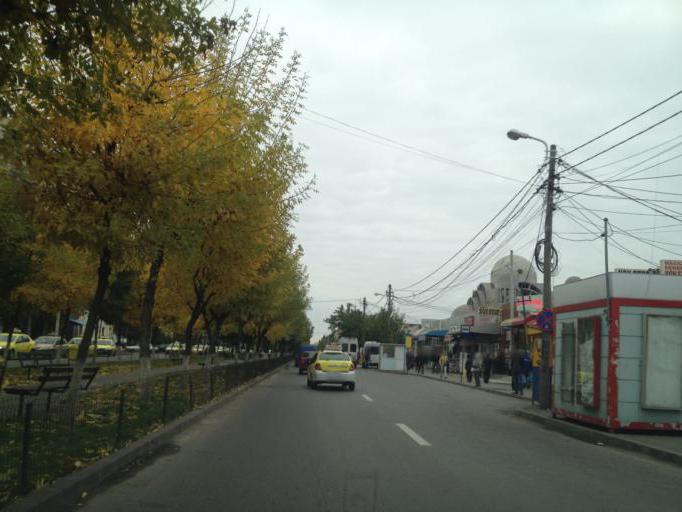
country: RO
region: Dolj
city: Craiova
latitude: 44.3372
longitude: 23.7763
